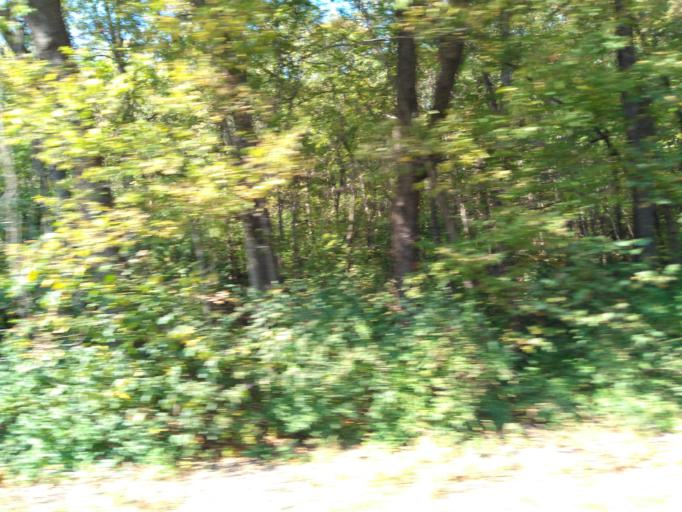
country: US
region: Missouri
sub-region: Saint Louis County
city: Valley Park
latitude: 38.5219
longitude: -90.5457
